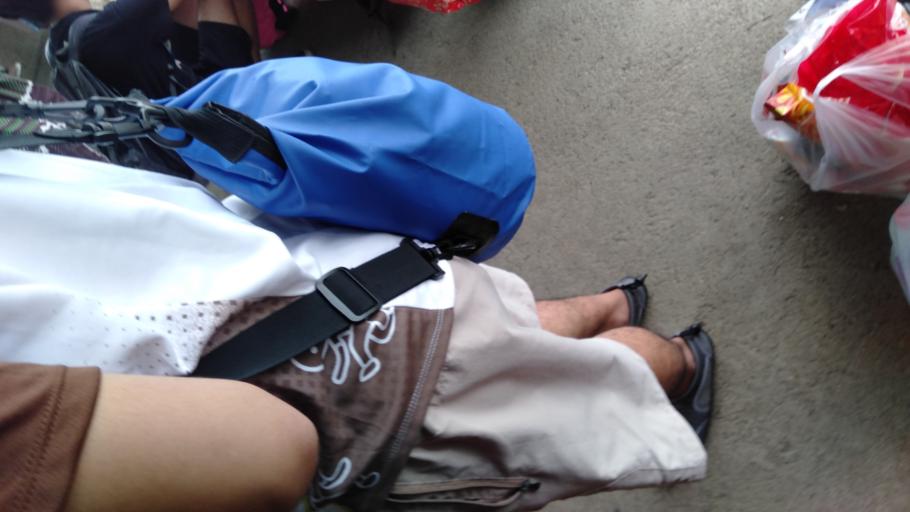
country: PH
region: Central Luzon
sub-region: Province of Bulacan
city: Bulacan
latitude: 14.7674
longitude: 120.8958
